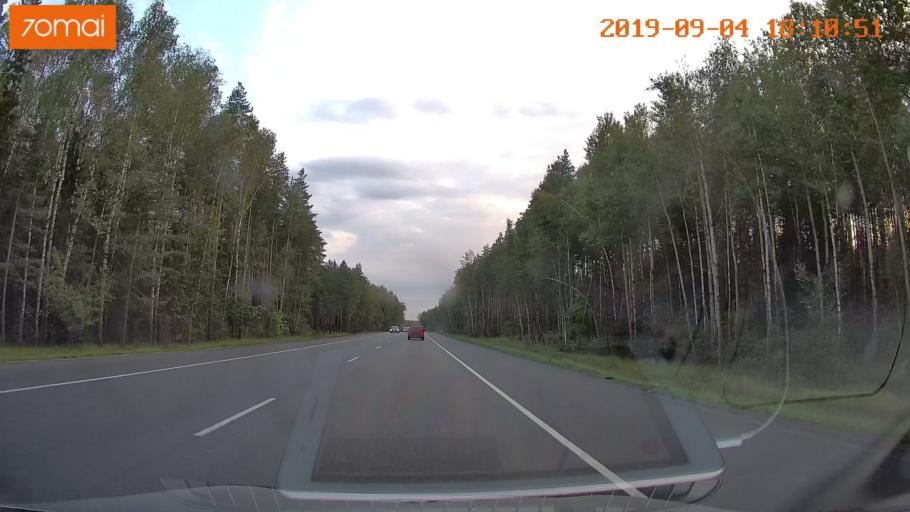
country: RU
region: Moskovskaya
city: Lopatinskiy
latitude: 55.3837
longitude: 38.7607
